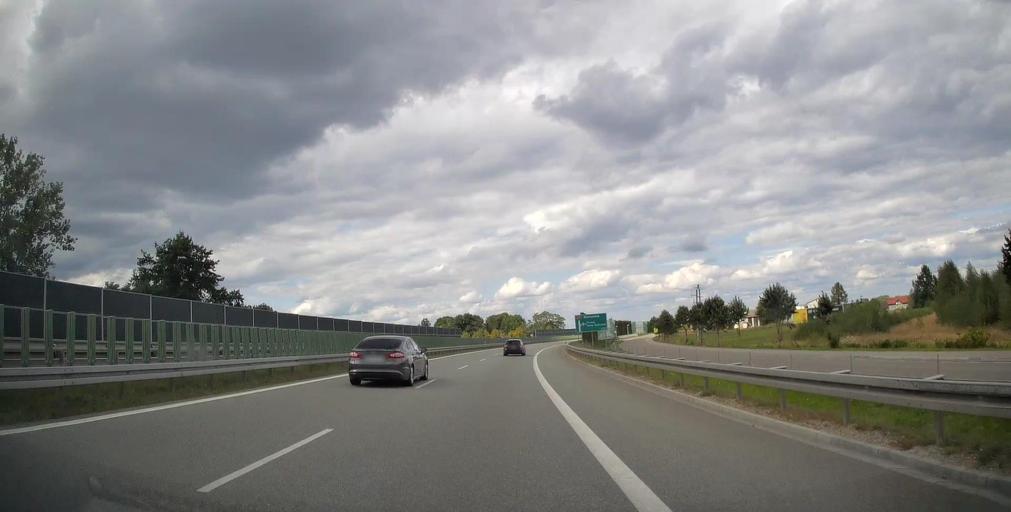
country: PL
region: Masovian Voivodeship
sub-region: Powiat bialobrzeski
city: Stara Blotnica
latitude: 51.5592
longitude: 21.0276
